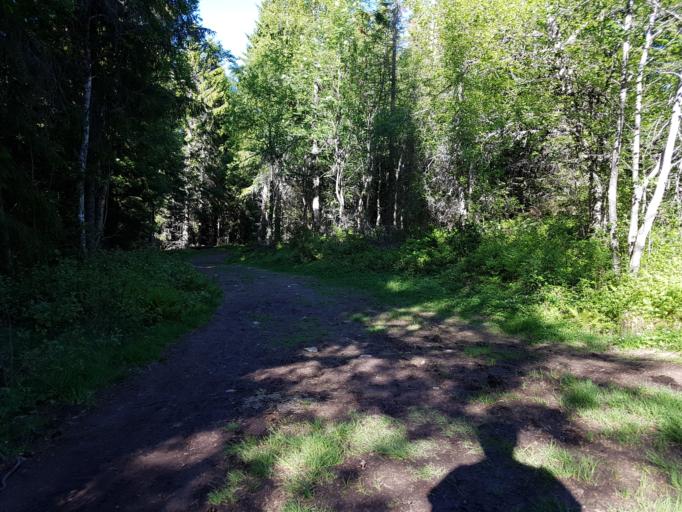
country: NO
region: Sor-Trondelag
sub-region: Trondheim
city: Trondheim
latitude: 63.4169
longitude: 10.3315
